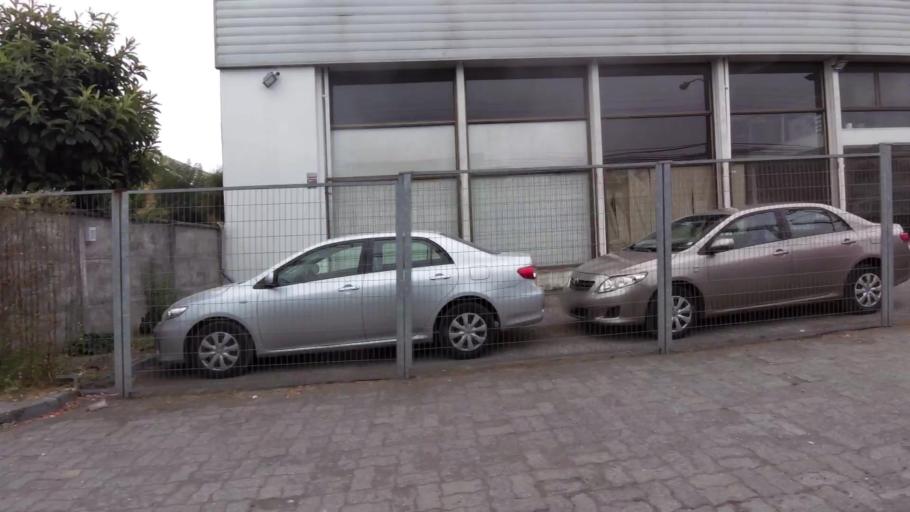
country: CL
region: Biobio
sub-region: Provincia de Concepcion
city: Concepcion
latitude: -36.8183
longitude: -73.0493
